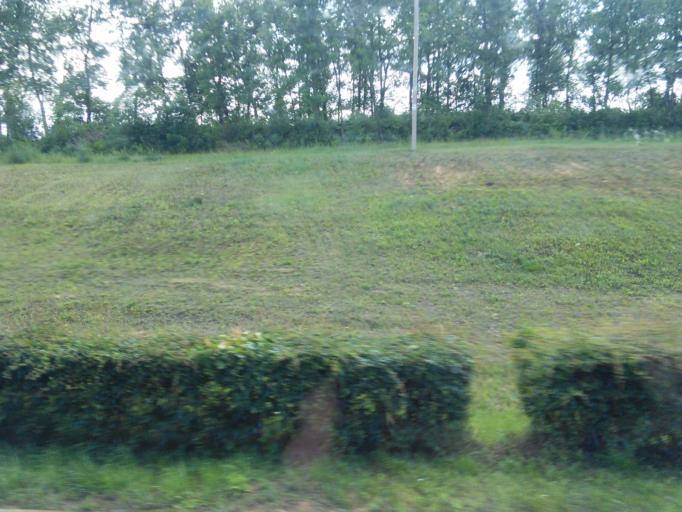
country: BY
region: Minsk
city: Maladzyechna
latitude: 54.2837
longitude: 26.9533
